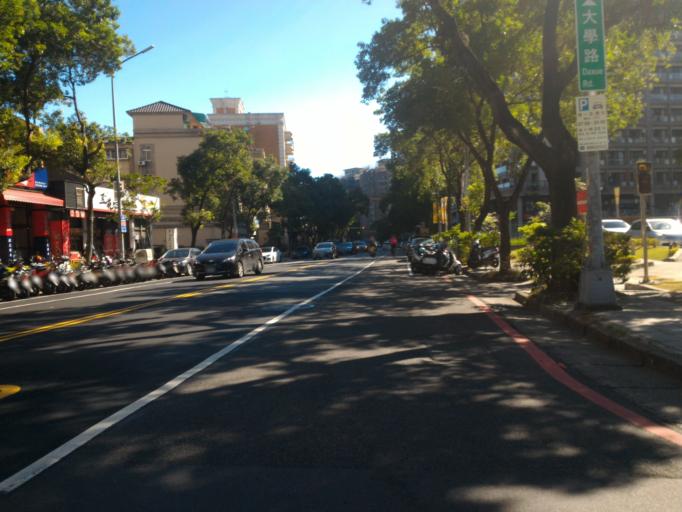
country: TW
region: Taiwan
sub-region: Taoyuan
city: Taoyuan
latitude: 24.9426
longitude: 121.3756
